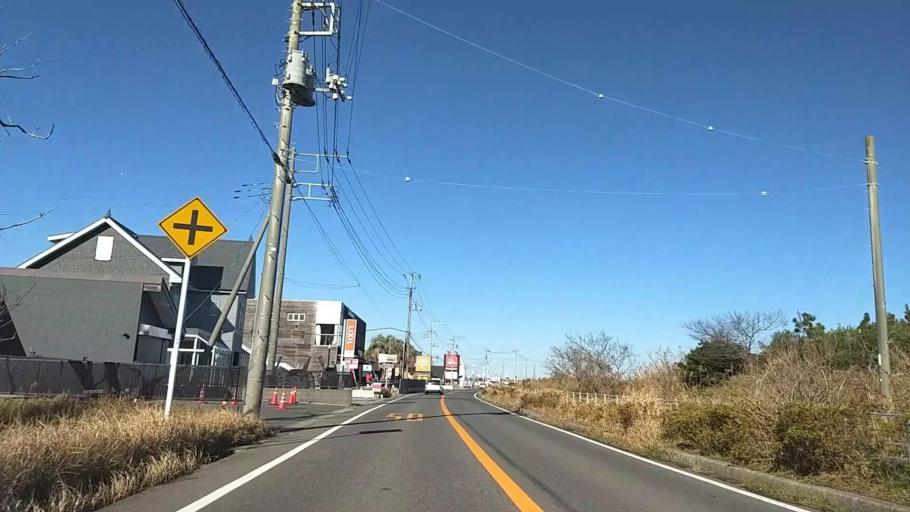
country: JP
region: Chiba
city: Ohara
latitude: 35.3449
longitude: 140.3903
